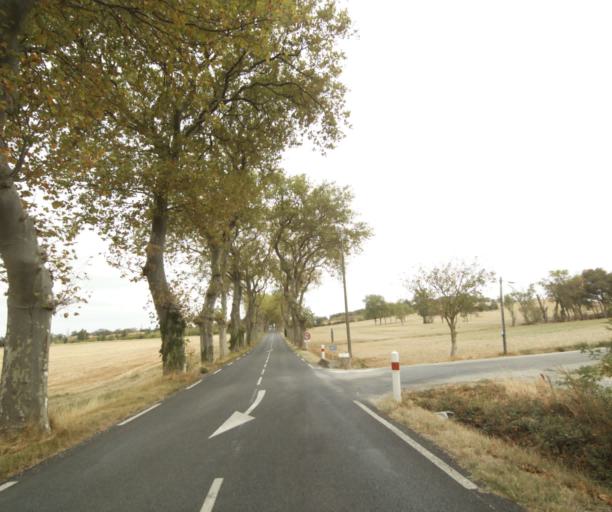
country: FR
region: Midi-Pyrenees
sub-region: Departement de la Haute-Garonne
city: Villefranche-de-Lauragais
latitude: 43.4075
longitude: 1.7305
